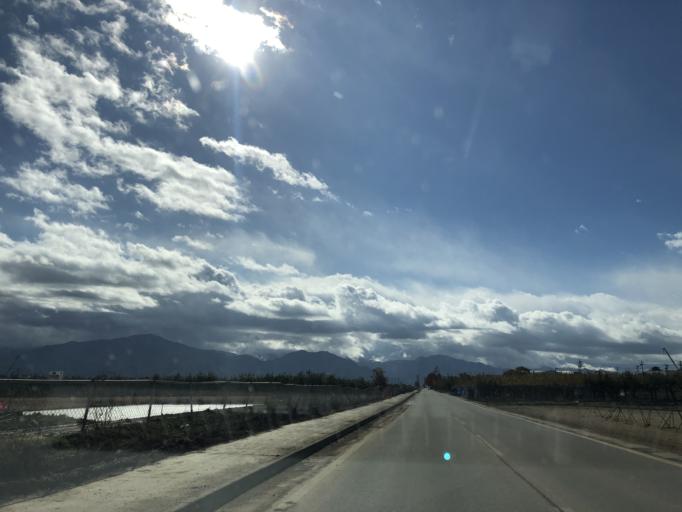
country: JP
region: Nagano
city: Suzaka
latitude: 36.6890
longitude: 138.2621
